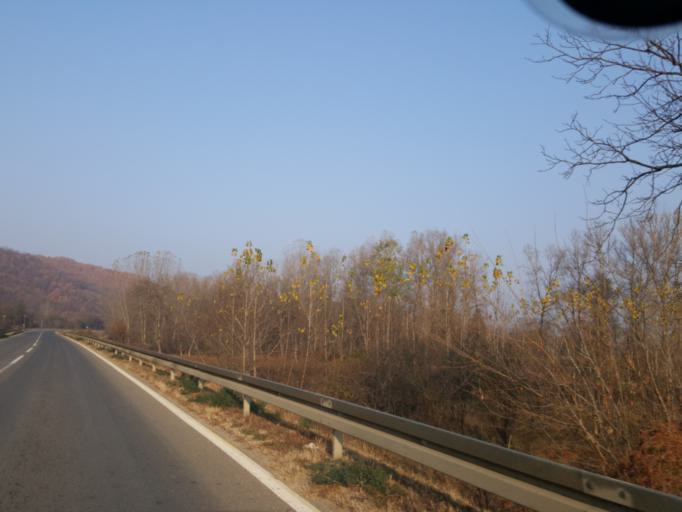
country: RS
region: Central Serbia
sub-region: Jablanicki Okrug
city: Vlasotince
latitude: 42.8951
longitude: 22.0527
